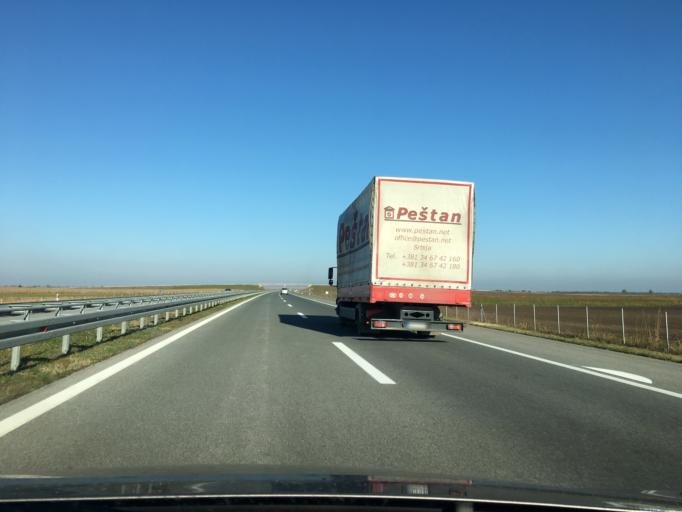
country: RS
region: Autonomna Pokrajina Vojvodina
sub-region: Severnobacki Okrug
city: Mali Igos
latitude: 45.7264
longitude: 19.7070
